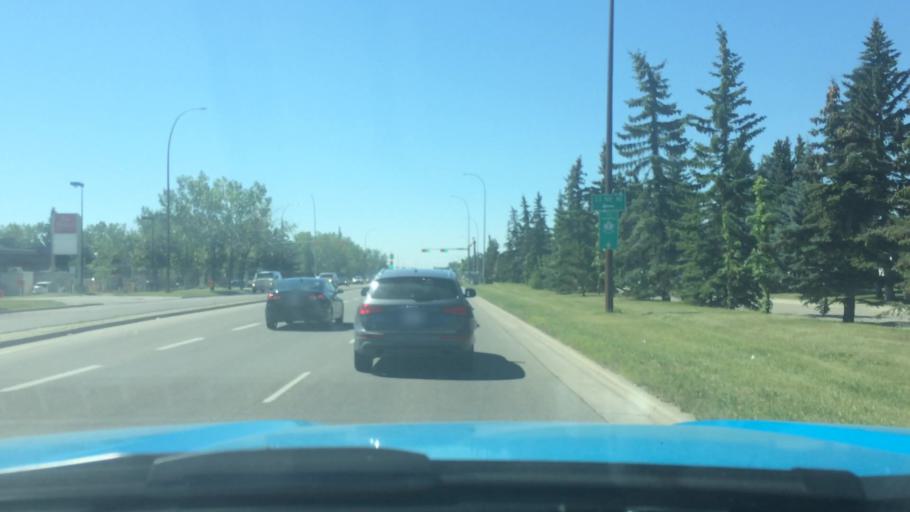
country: CA
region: Alberta
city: Calgary
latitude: 51.0752
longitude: -113.9585
